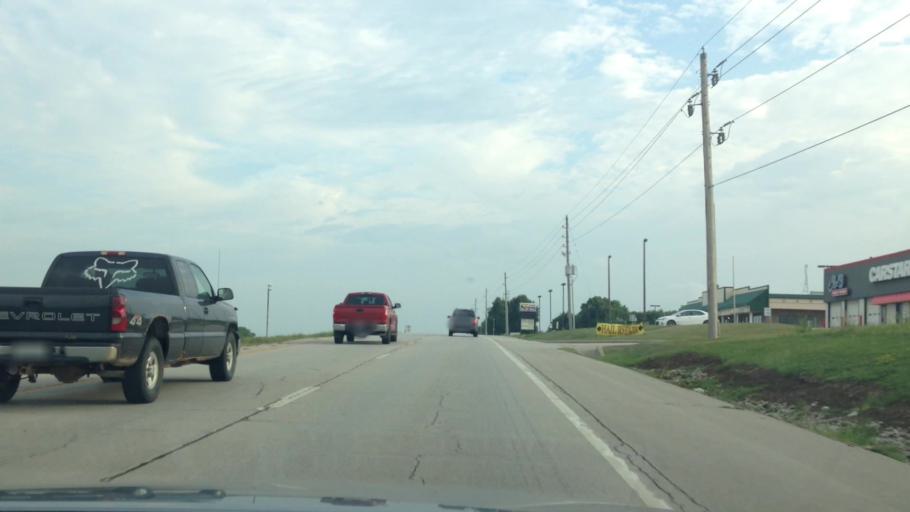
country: US
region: Missouri
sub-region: Clay County
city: Smithville
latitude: 39.3571
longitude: -94.5841
